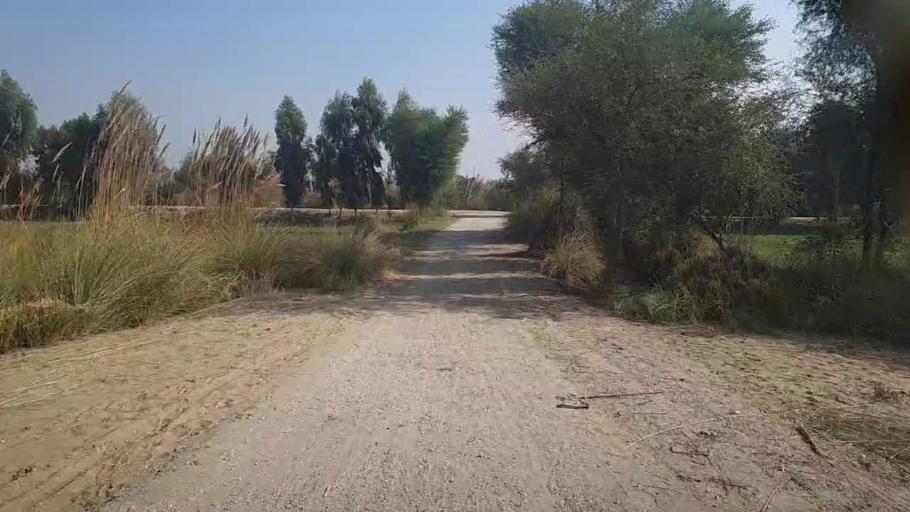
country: PK
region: Sindh
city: Kandiari
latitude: 26.9377
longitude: 68.5507
